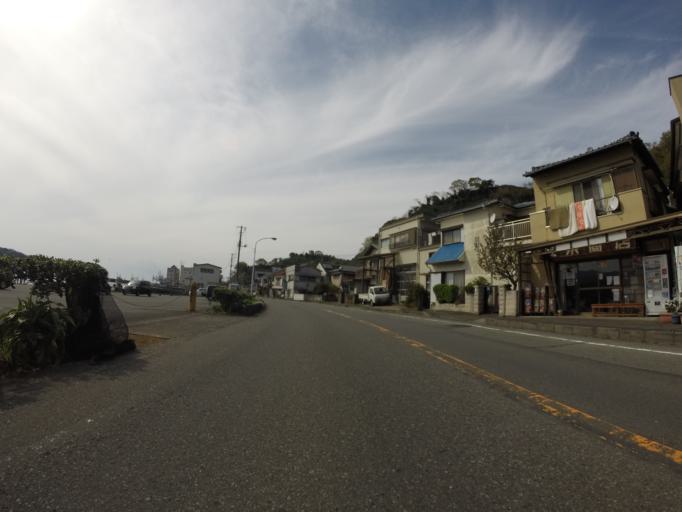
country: JP
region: Shizuoka
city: Numazu
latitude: 35.0253
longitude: 138.8985
